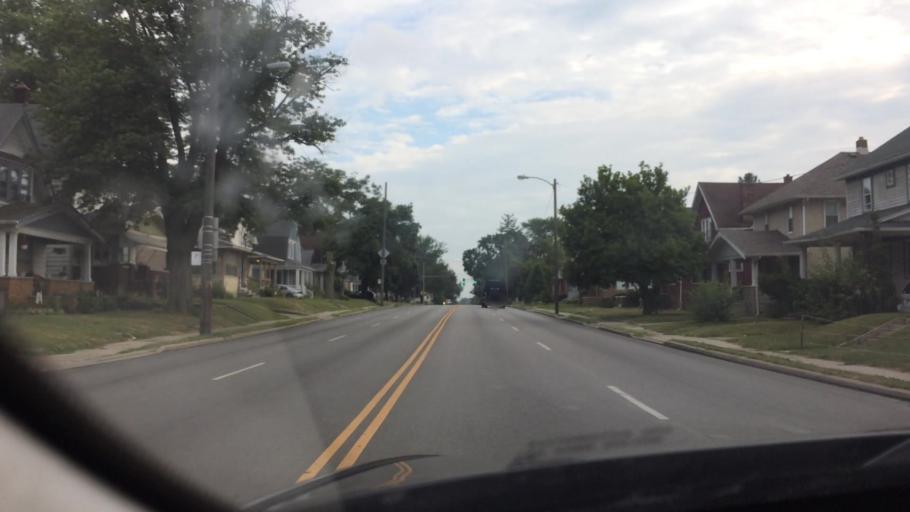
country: US
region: Ohio
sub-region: Wood County
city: Rossford
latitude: 41.6325
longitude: -83.5910
